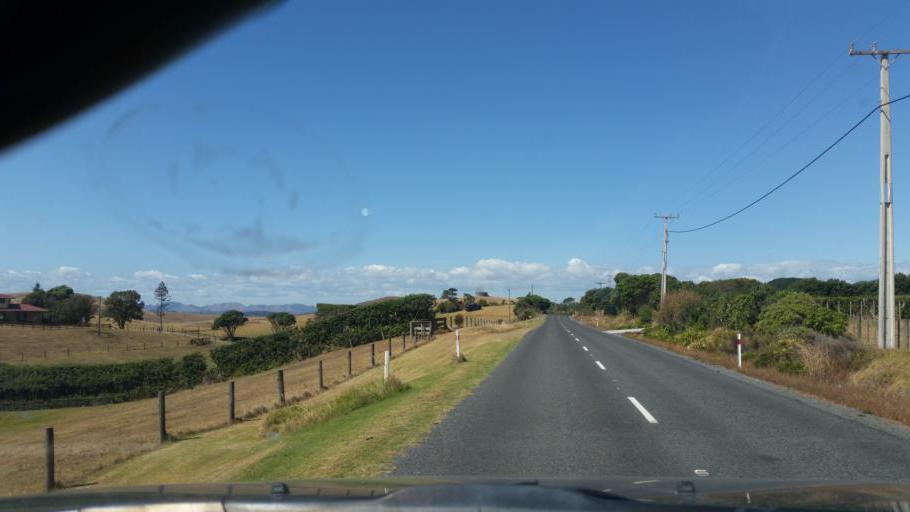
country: NZ
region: Northland
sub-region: Kaipara District
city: Dargaville
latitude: -35.9505
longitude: 173.7536
